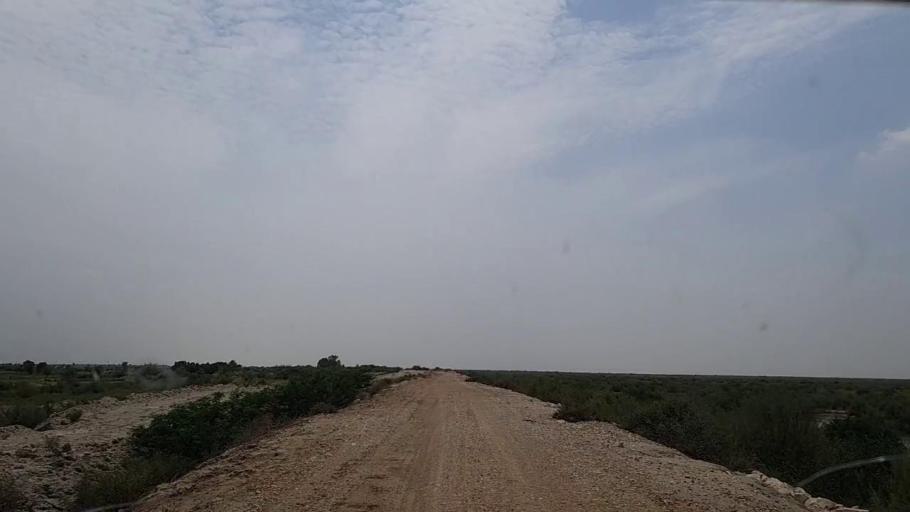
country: PK
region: Sindh
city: Phulji
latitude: 26.8611
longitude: 67.6369
